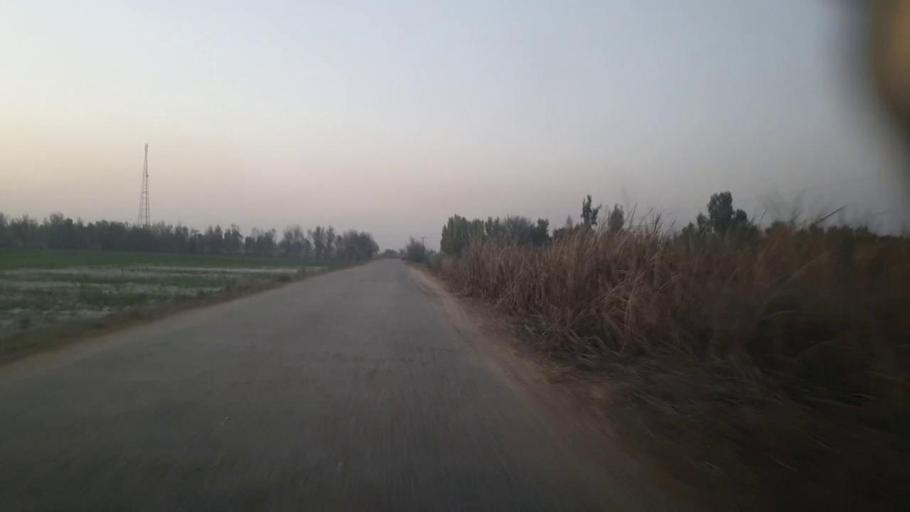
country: PK
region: Sindh
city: Kandiari
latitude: 26.6784
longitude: 68.9443
